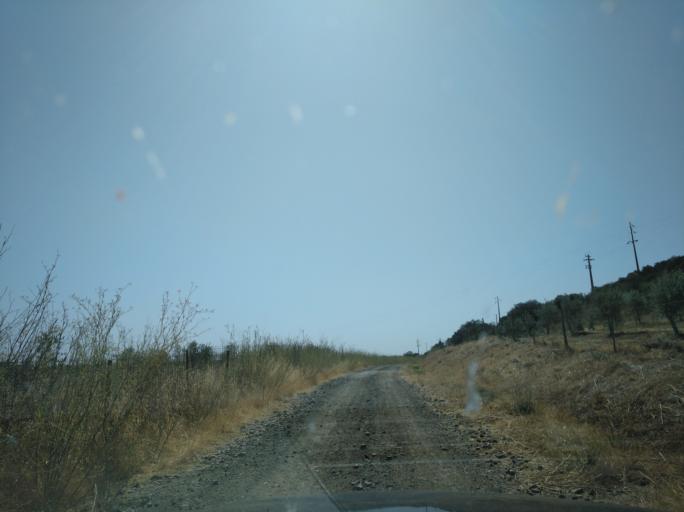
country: PT
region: Portalegre
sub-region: Campo Maior
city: Campo Maior
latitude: 39.0604
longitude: -7.0085
